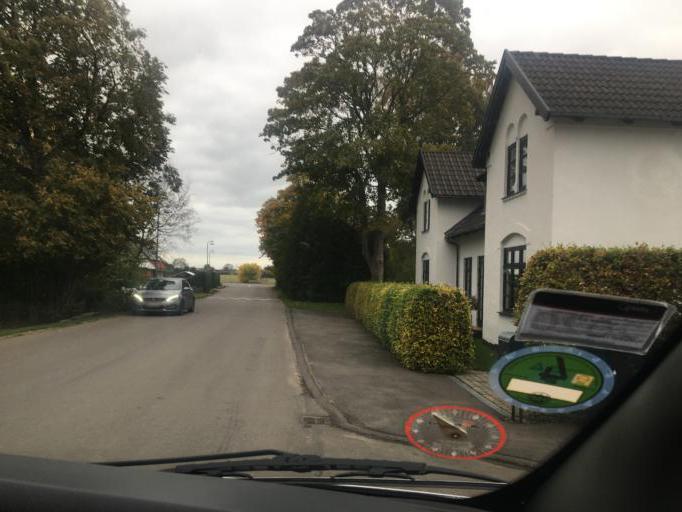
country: DK
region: Zealand
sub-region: Koge Kommune
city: Bjaeverskov
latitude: 55.4273
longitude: 11.9851
